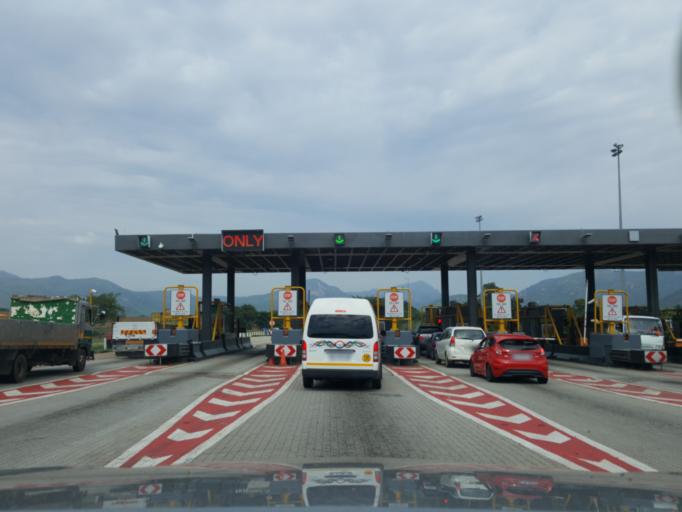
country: SZ
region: Hhohho
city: Ntfonjeni
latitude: -25.5363
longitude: 31.3450
